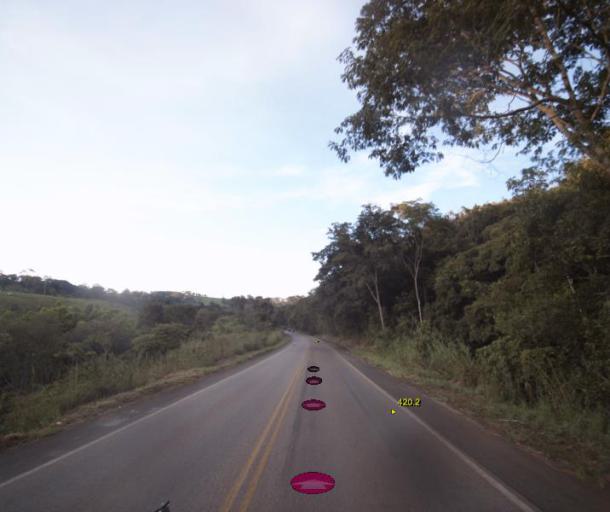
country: BR
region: Goias
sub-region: Abadiania
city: Abadiania
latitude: -16.1259
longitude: -48.8948
